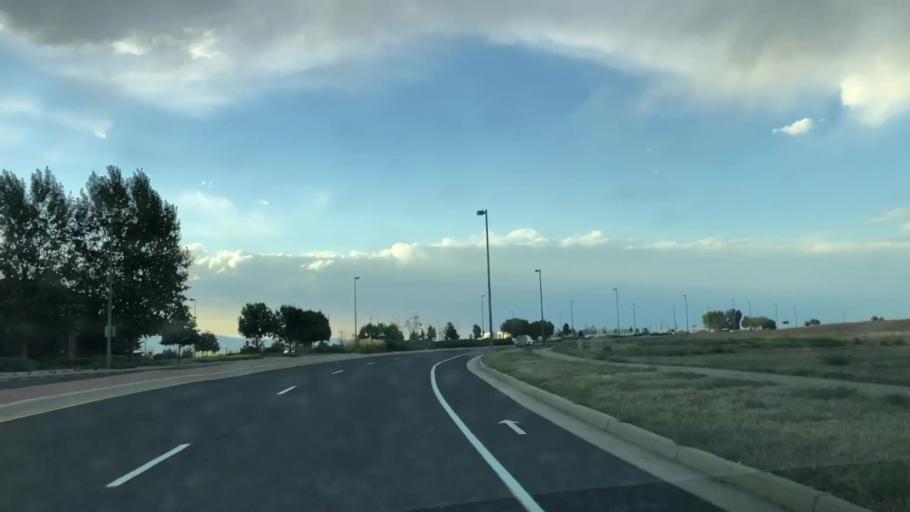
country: US
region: Colorado
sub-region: Larimer County
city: Loveland
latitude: 40.4210
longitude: -104.9969
